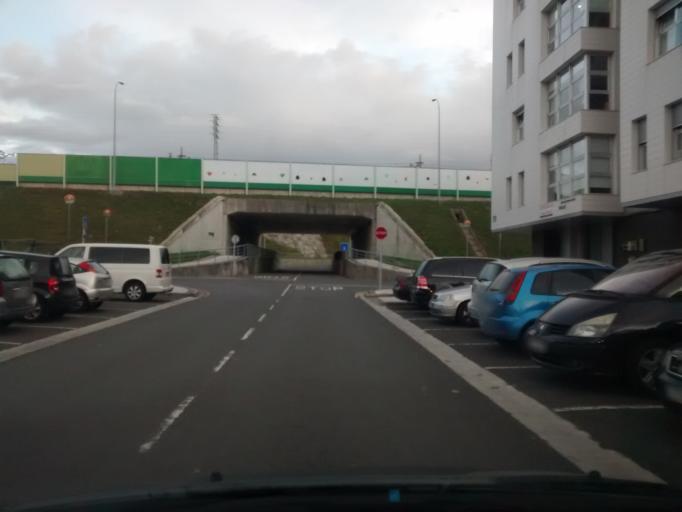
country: ES
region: Basque Country
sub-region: Provincia de Guipuzcoa
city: Zumaia
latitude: 43.2899
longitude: -2.2551
